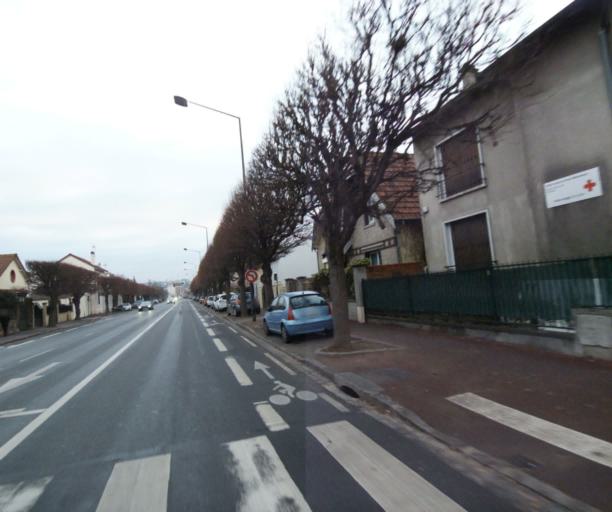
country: FR
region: Ile-de-France
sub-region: Departement des Hauts-de-Seine
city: Rueil-Malmaison
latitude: 48.8854
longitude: 2.1765
